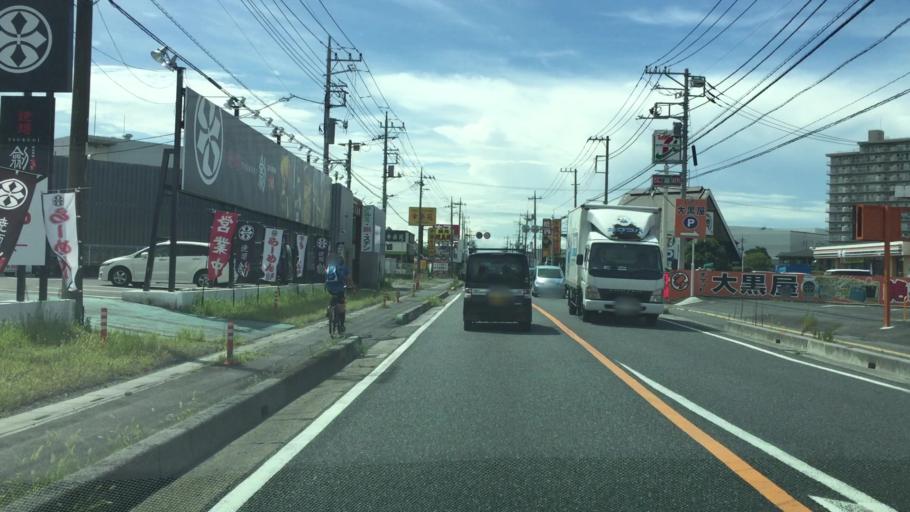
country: JP
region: Chiba
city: Nagareyama
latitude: 35.8481
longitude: 139.8687
